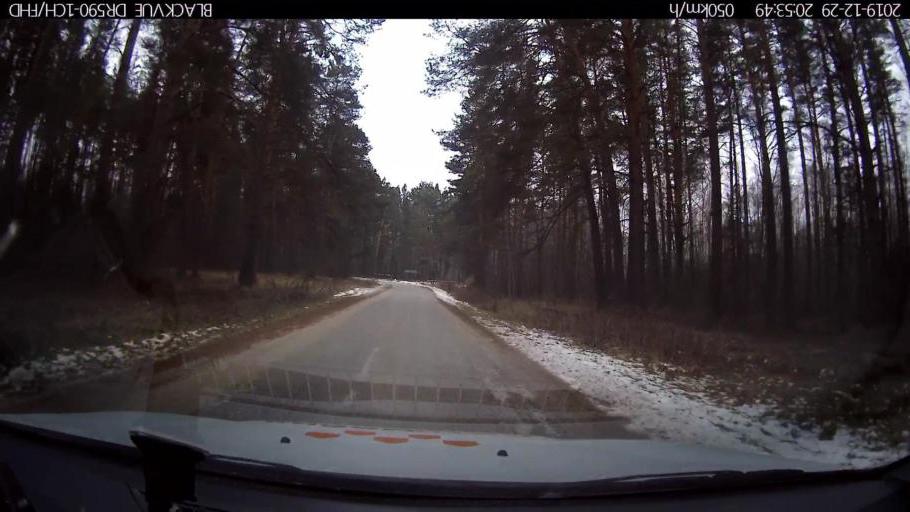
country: RU
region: Nizjnij Novgorod
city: Afonino
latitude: 56.1684
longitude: 43.9871
